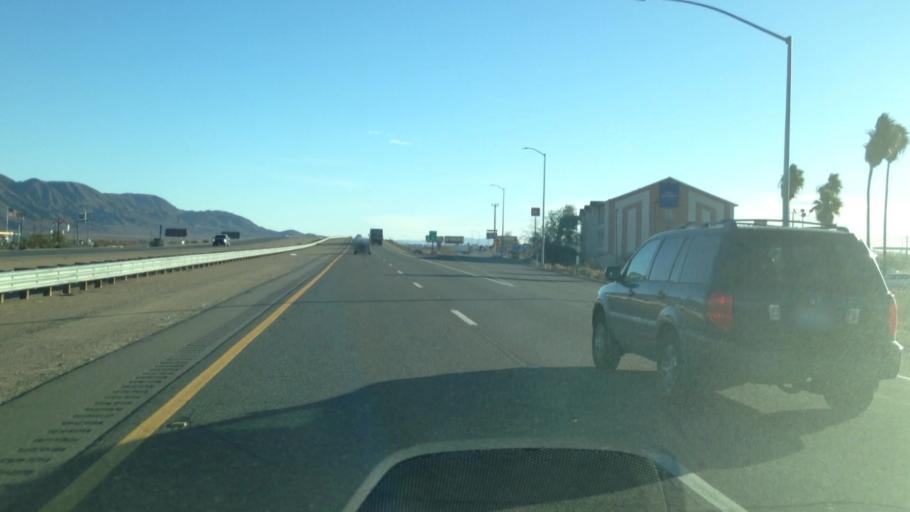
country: US
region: California
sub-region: San Bernardino County
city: Barstow
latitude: 34.9023
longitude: -116.8906
